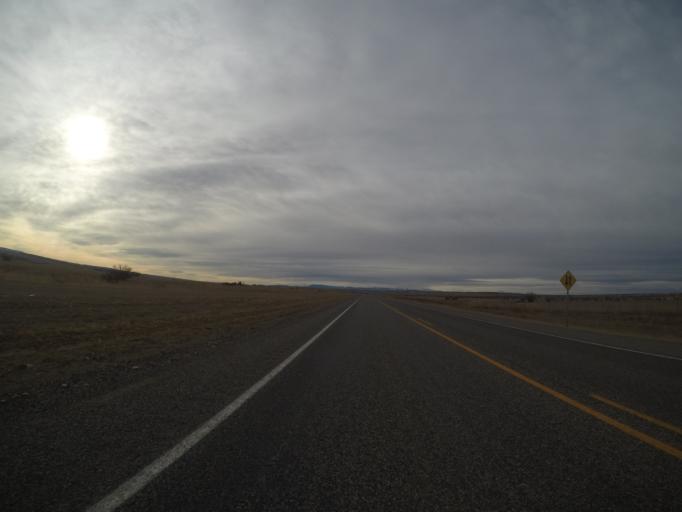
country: US
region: Montana
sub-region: Yellowstone County
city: Laurel
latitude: 45.5906
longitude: -108.8337
